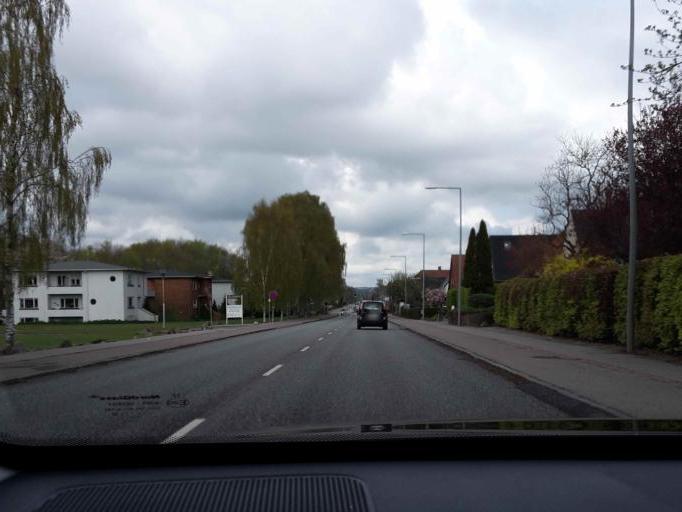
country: DK
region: South Denmark
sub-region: Vejle Kommune
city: Vejle
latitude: 55.6908
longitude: 9.5494
